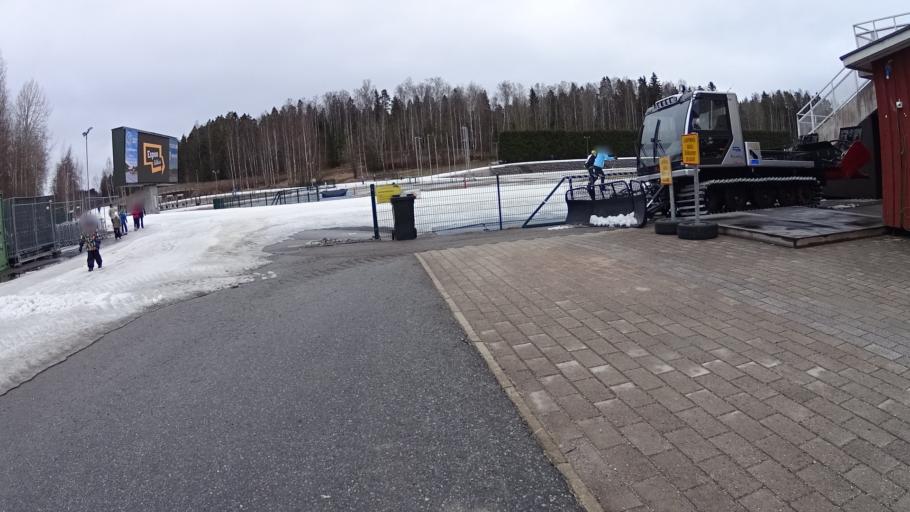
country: FI
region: Uusimaa
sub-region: Helsinki
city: Kilo
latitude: 60.2255
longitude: 24.7975
